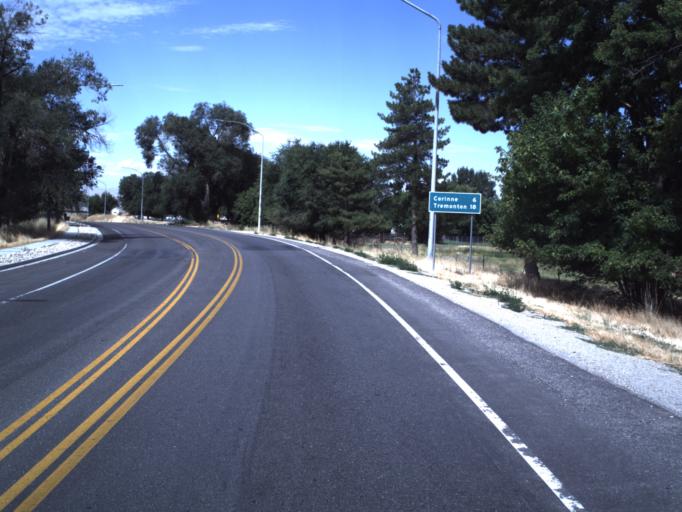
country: US
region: Utah
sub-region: Box Elder County
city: Brigham City
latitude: 41.5296
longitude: -112.0184
